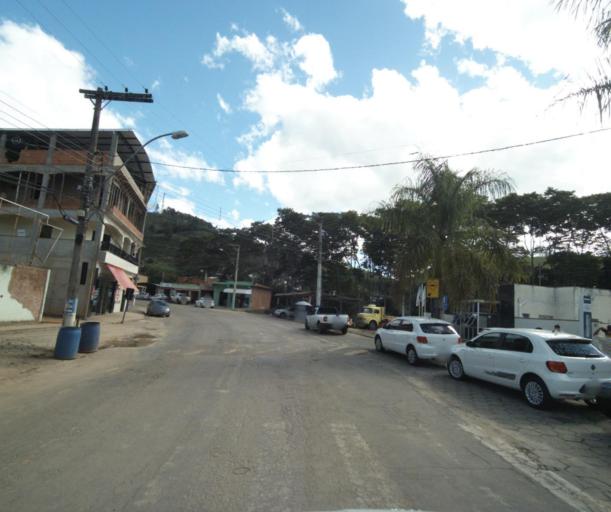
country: BR
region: Espirito Santo
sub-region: Irupi
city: Irupi
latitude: -20.5386
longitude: -41.6656
